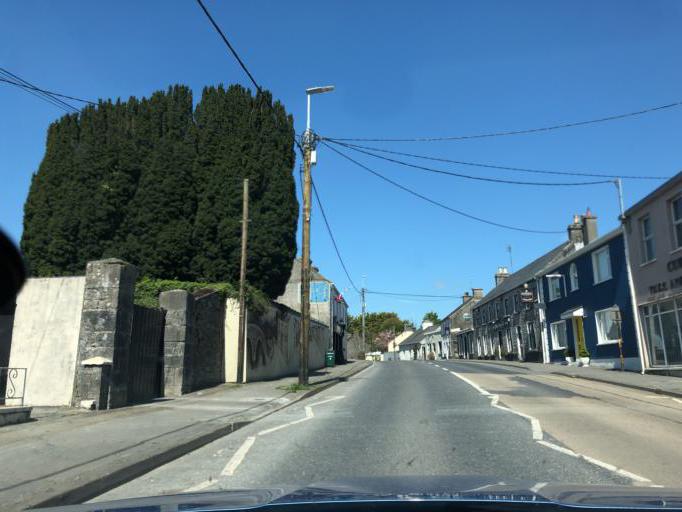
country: IE
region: Connaught
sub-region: County Galway
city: Athenry
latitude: 53.2295
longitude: -8.7341
